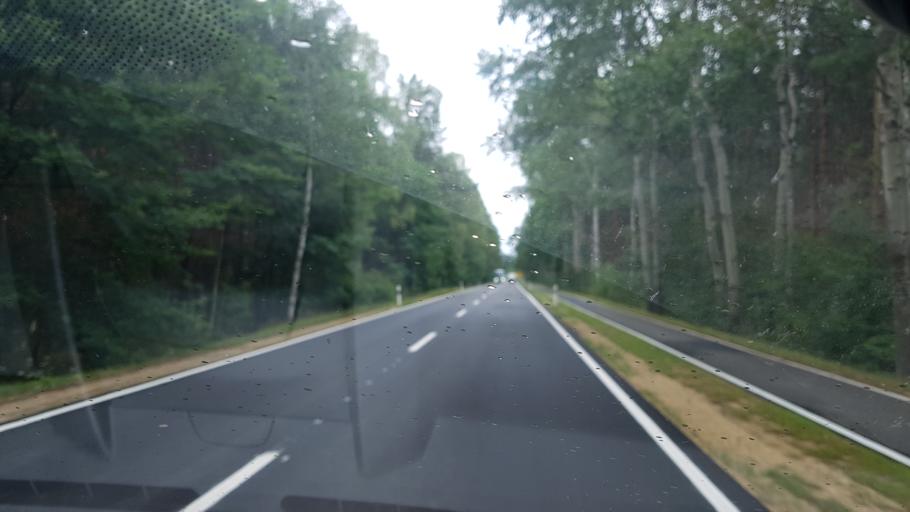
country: DE
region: Saxony
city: Niesky
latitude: 51.3115
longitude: 14.8216
